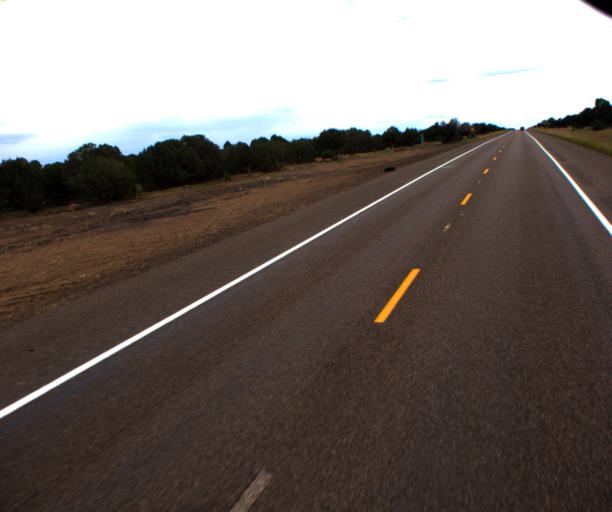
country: US
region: Arizona
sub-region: Navajo County
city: White Mountain Lake
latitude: 34.3098
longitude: -110.0387
